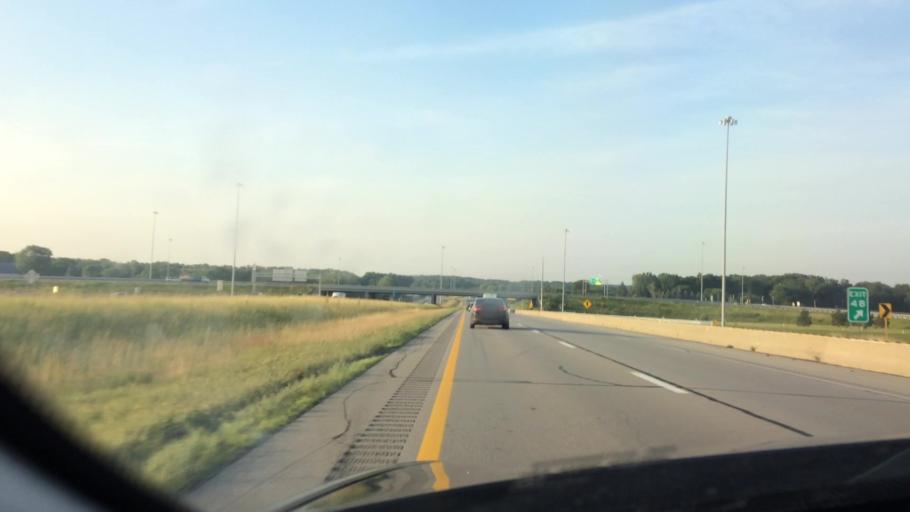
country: US
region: Ohio
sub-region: Lucas County
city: Maumee
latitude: 41.5565
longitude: -83.6872
